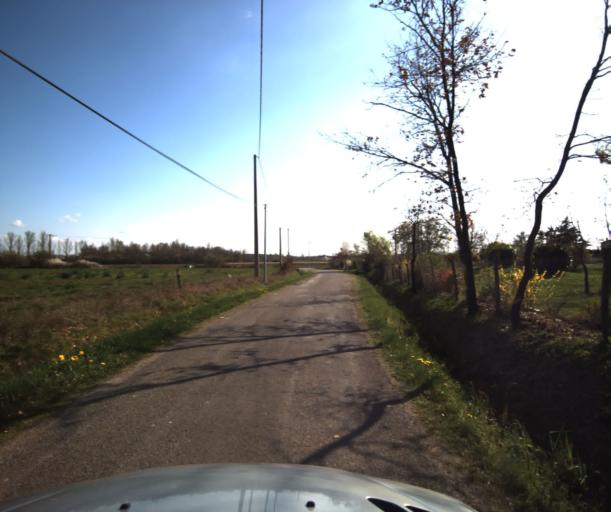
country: FR
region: Midi-Pyrenees
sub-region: Departement du Tarn-et-Garonne
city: Bressols
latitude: 43.9452
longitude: 1.3117
